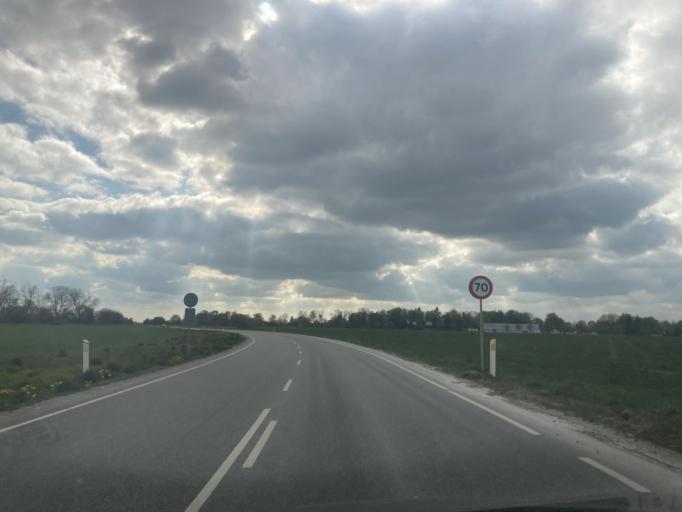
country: DK
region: Zealand
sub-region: Roskilde Kommune
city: Vindinge
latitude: 55.5985
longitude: 12.1191
